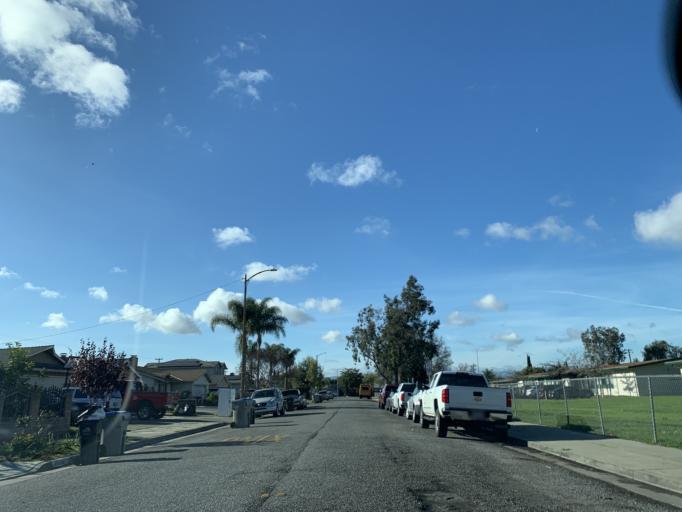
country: US
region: California
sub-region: Santa Clara County
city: Alum Rock
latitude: 37.3502
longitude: -121.8308
